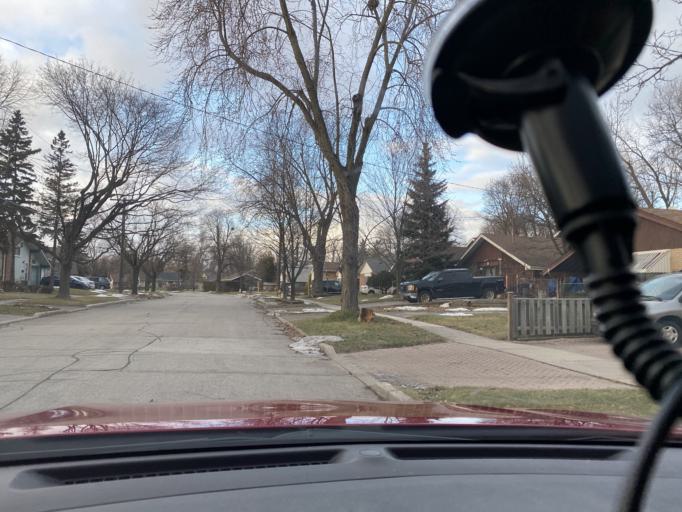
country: CA
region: Ontario
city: Scarborough
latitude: 43.7648
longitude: -79.2072
